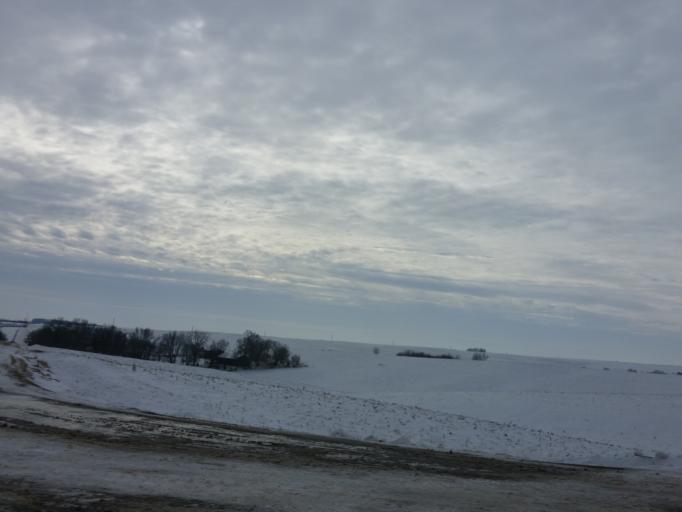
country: US
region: Iowa
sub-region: Dubuque County
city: Peosta
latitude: 42.3821
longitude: -90.7632
